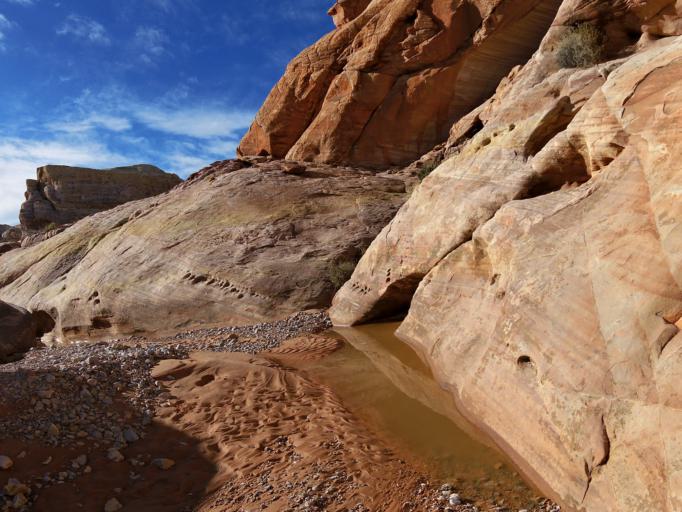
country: US
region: Nevada
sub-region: Clark County
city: Moapa Valley
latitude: 36.4805
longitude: -114.5287
